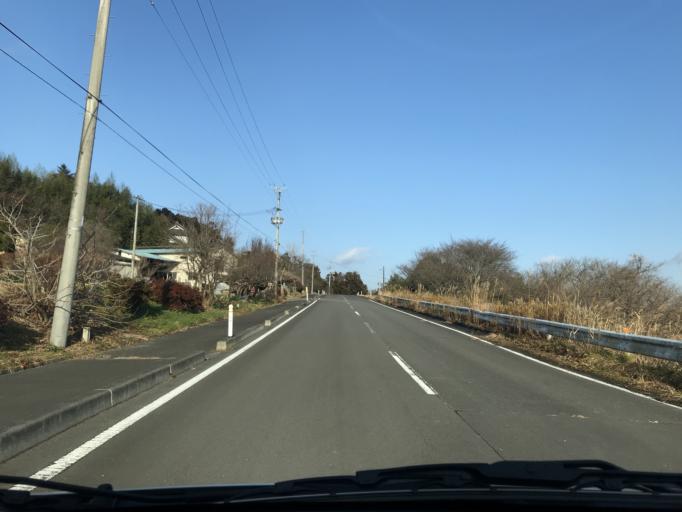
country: JP
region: Miyagi
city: Wakuya
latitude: 38.6844
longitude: 141.1153
